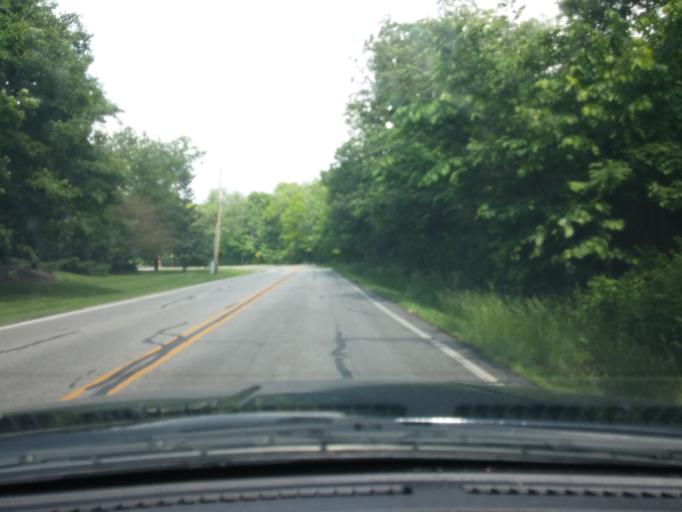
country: US
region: Indiana
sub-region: Tippecanoe County
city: West Lafayette
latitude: 40.4706
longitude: -86.8985
